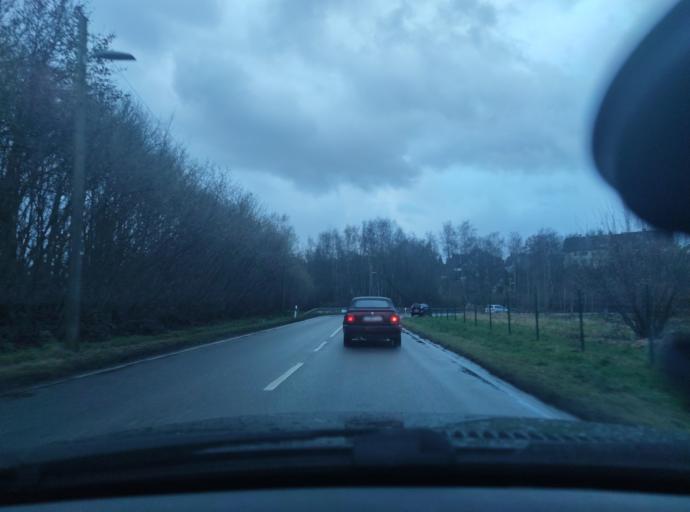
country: DE
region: North Rhine-Westphalia
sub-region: Regierungsbezirk Dusseldorf
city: Essen
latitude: 51.4395
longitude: 7.0799
